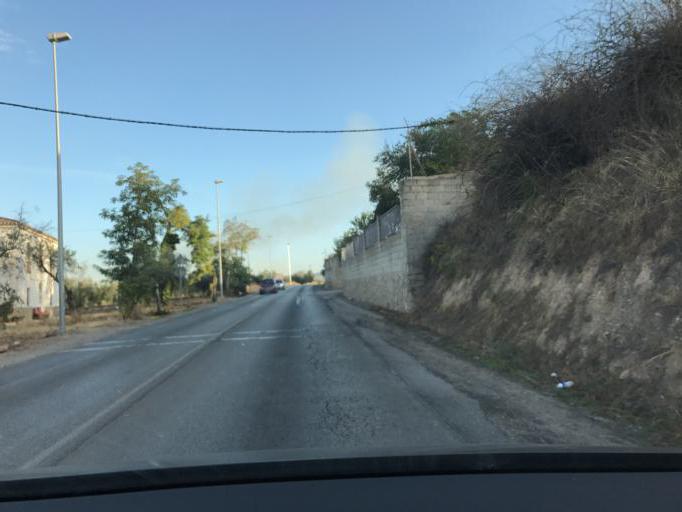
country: ES
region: Andalusia
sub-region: Provincia de Granada
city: Pulianas
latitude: 37.2231
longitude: -3.6100
